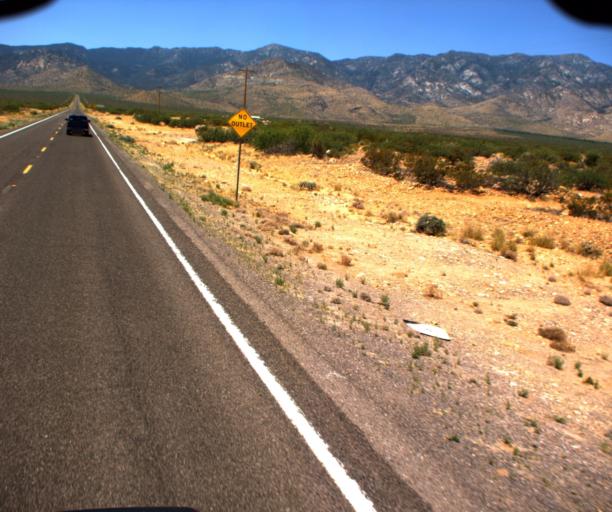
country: US
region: Arizona
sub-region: Graham County
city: Swift Trail Junction
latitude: 32.7151
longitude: -109.7291
